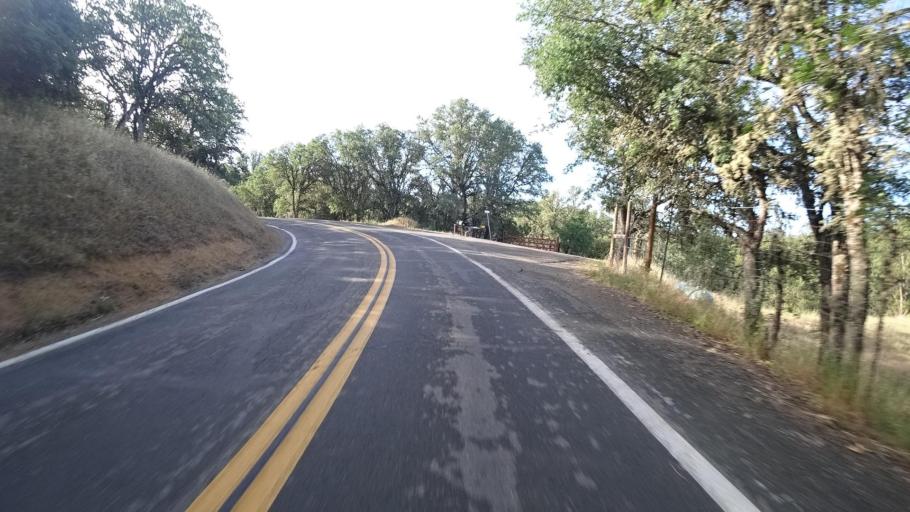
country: US
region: California
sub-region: Lake County
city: North Lakeport
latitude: 39.0705
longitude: -122.9283
